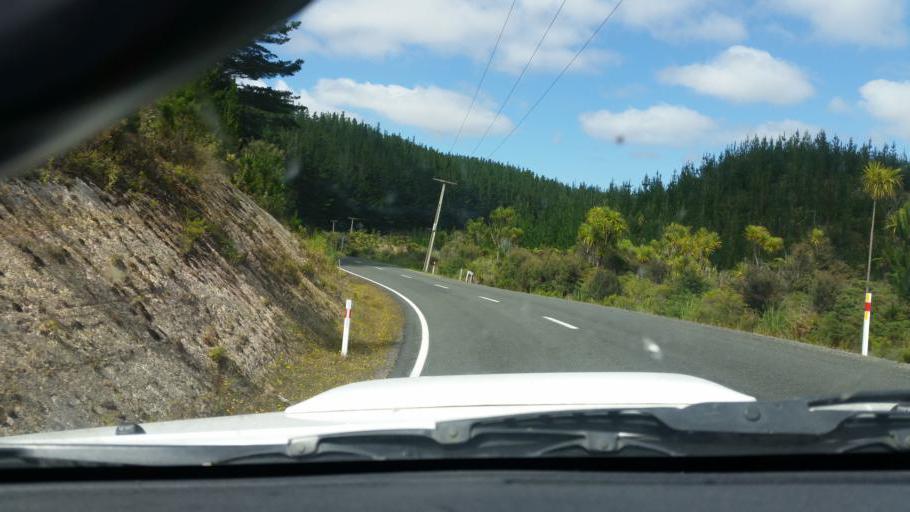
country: NZ
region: Northland
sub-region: Kaipara District
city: Dargaville
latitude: -35.8186
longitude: 173.7110
